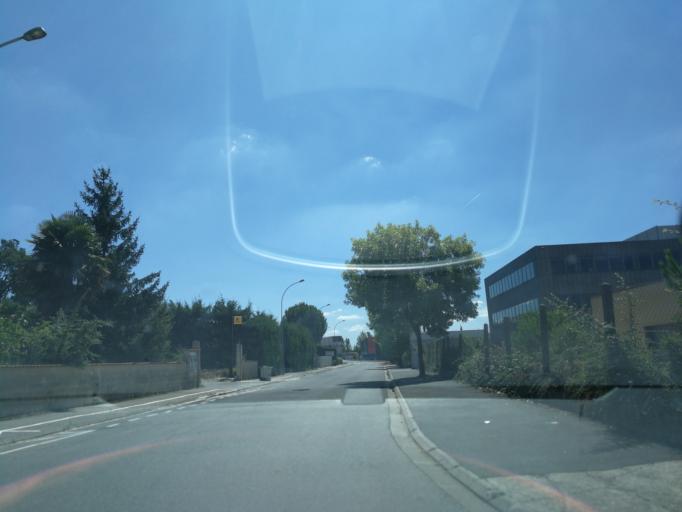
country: FR
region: Midi-Pyrenees
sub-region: Departement de la Haute-Garonne
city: Balma
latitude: 43.6283
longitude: 1.4882
